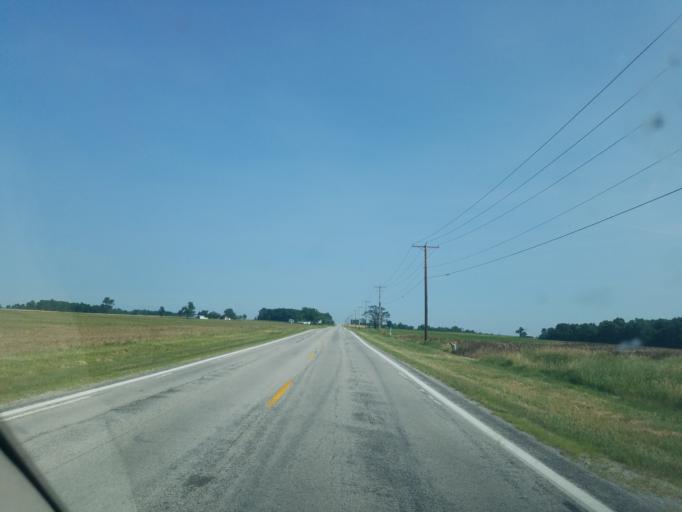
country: US
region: Ohio
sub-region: Wyandot County
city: Carey
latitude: 41.0210
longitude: -83.2912
